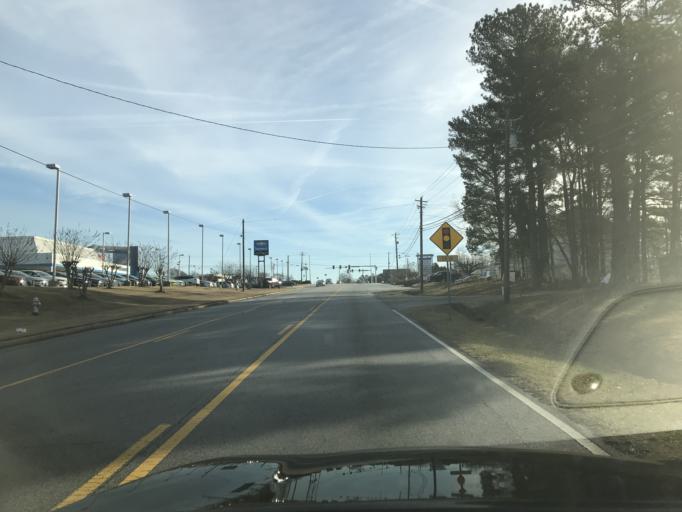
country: US
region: Georgia
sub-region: Clayton County
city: Morrow
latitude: 33.5532
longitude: -84.3497
